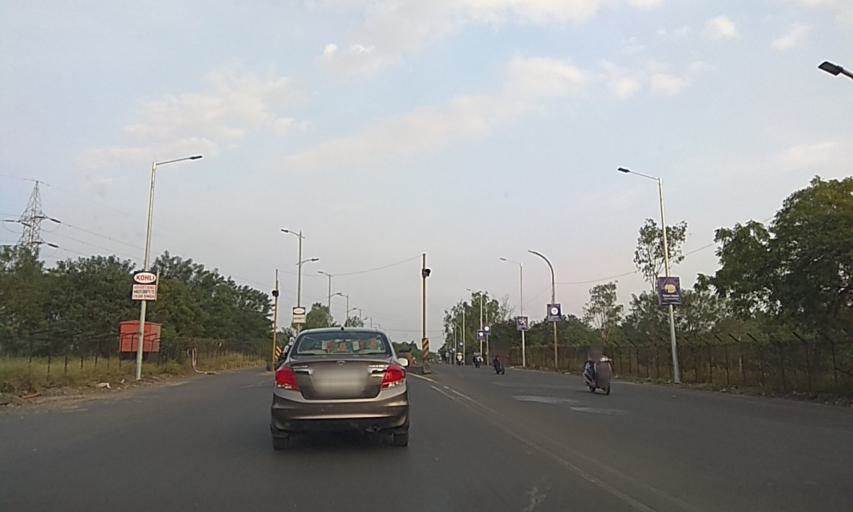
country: IN
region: Maharashtra
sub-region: Pune Division
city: Pimpri
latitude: 18.5875
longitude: 73.7880
